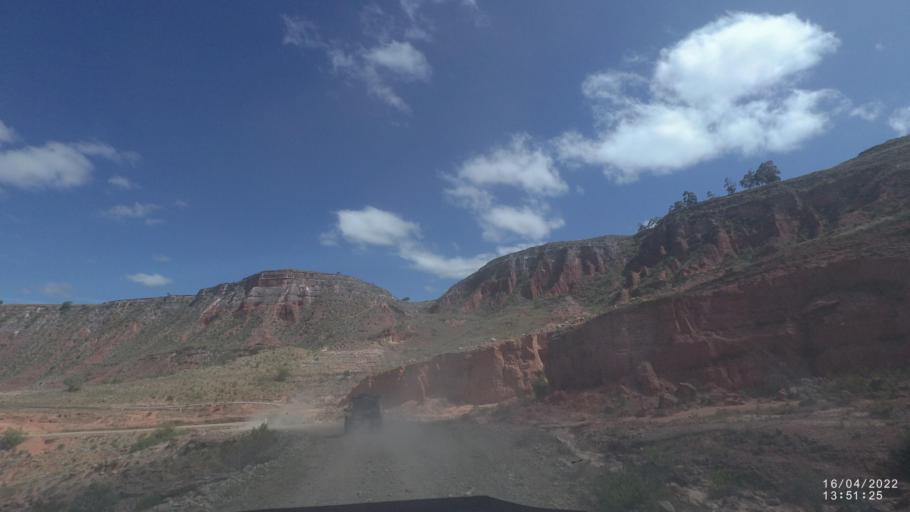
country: BO
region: Cochabamba
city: Mizque
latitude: -18.0192
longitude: -65.5751
